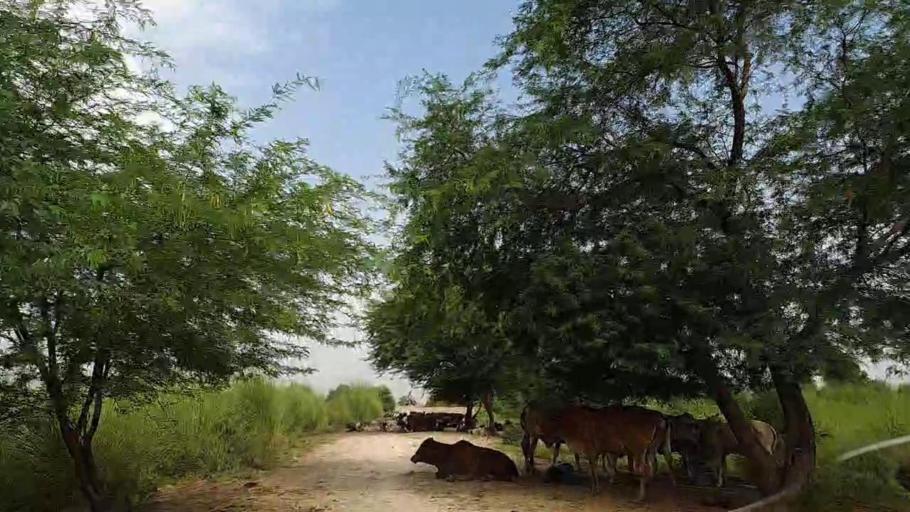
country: PK
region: Sindh
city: Khanpur
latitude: 27.8254
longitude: 69.5179
